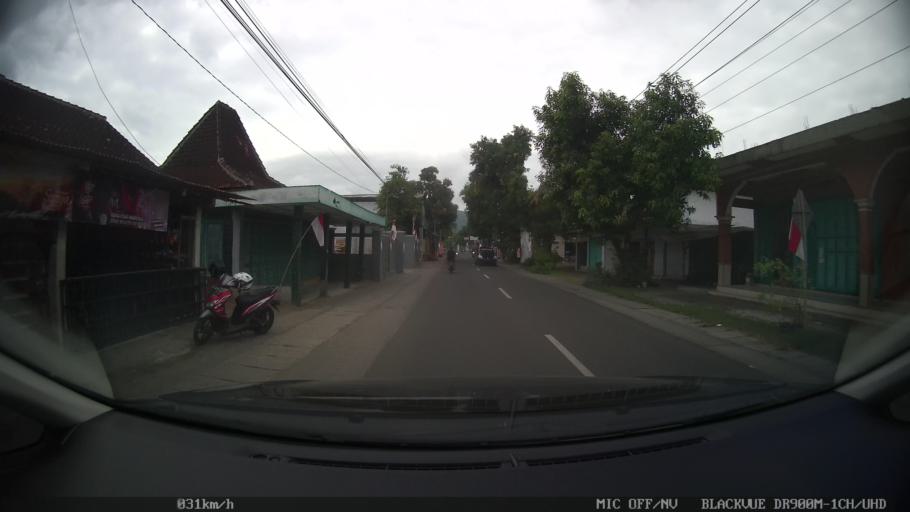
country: ID
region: Daerah Istimewa Yogyakarta
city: Sewon
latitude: -7.8792
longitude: 110.4158
